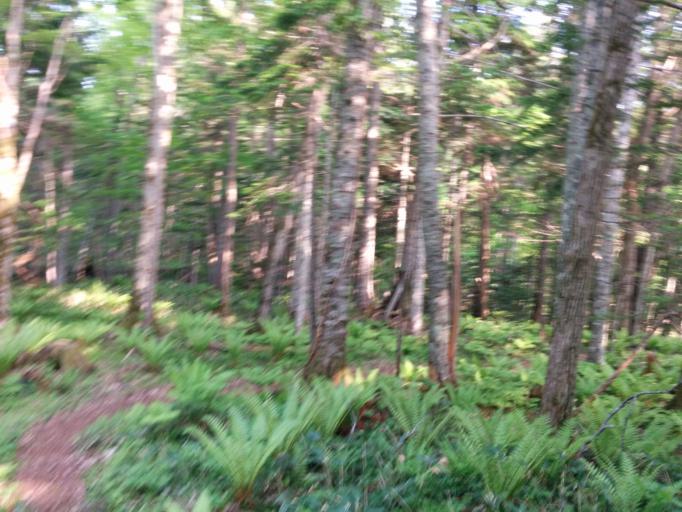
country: JP
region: Hokkaido
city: Bihoro
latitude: 43.4358
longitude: 144.1027
